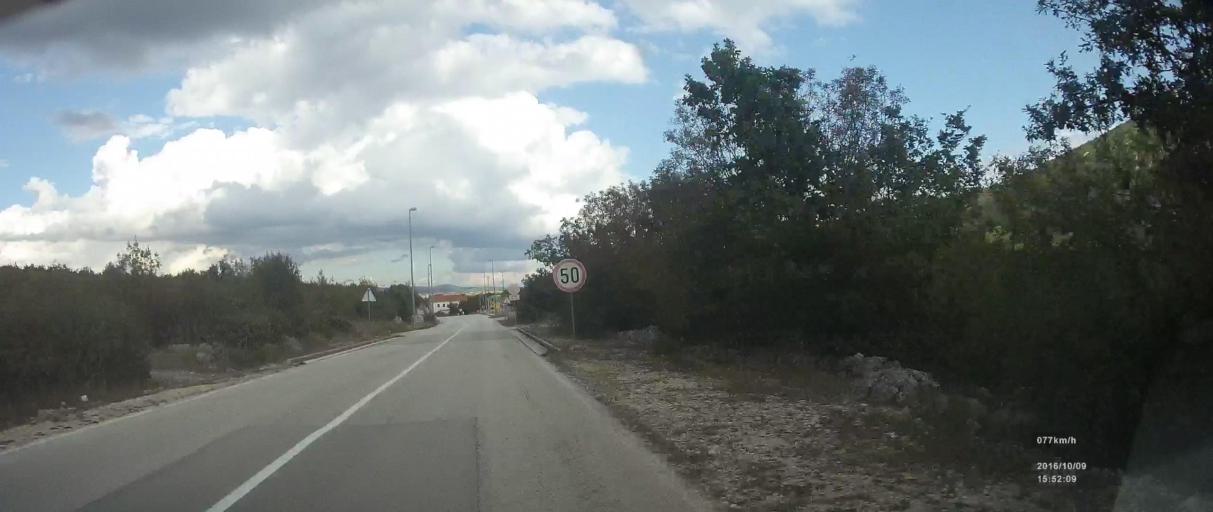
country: HR
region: Splitsko-Dalmatinska
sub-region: Grad Trogir
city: Trogir
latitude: 43.6076
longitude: 16.2207
